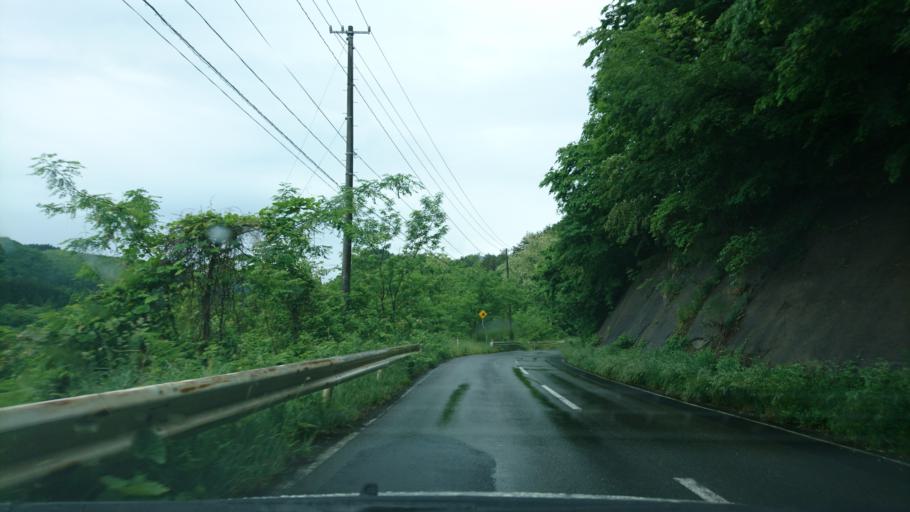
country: JP
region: Iwate
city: Ichinoseki
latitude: 38.9741
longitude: 140.9866
